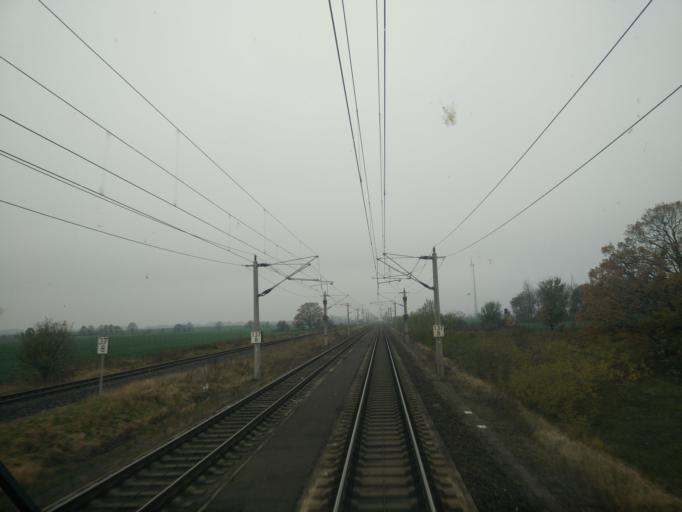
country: DE
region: Brandenburg
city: Nauen
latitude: 52.5667
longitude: 12.8353
